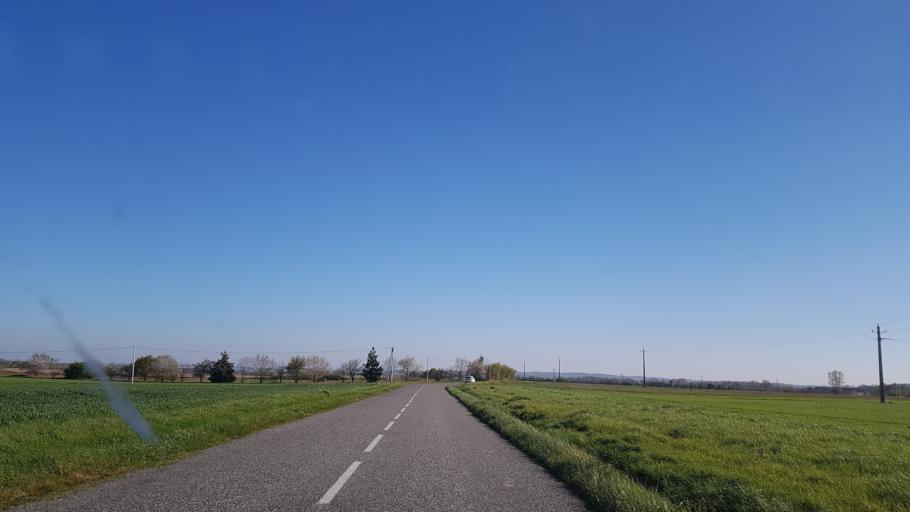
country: FR
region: Languedoc-Roussillon
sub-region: Departement de l'Aude
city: Belpech
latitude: 43.1550
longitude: 1.7069
